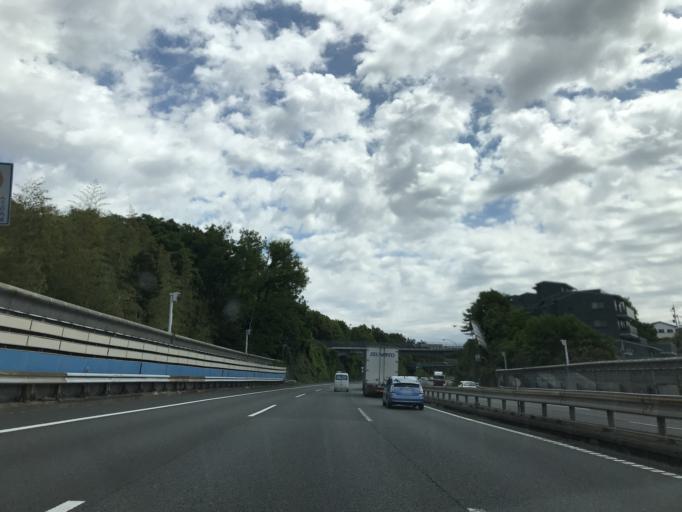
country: JP
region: Tokyo
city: Chofugaoka
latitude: 35.6282
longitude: 139.6108
